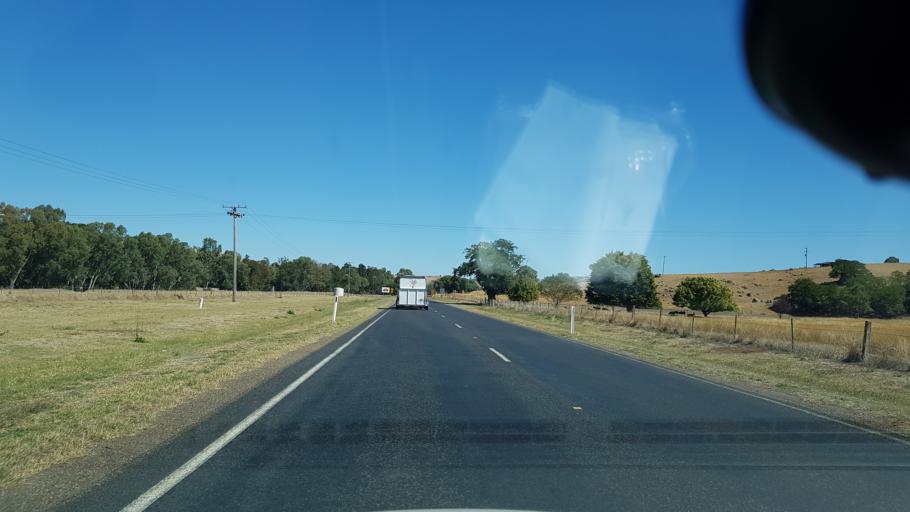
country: AU
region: New South Wales
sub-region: Gundagai
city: Gundagai
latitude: -34.8213
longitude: 148.3512
